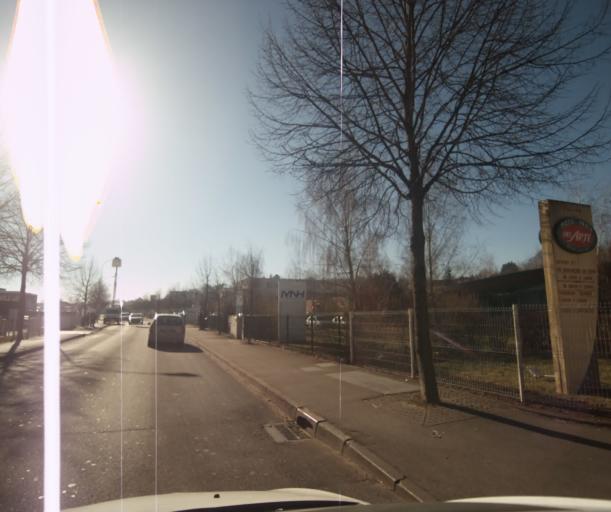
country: FR
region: Franche-Comte
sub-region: Departement du Doubs
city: Avanne-Aveney
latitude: 47.2170
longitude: 5.9637
